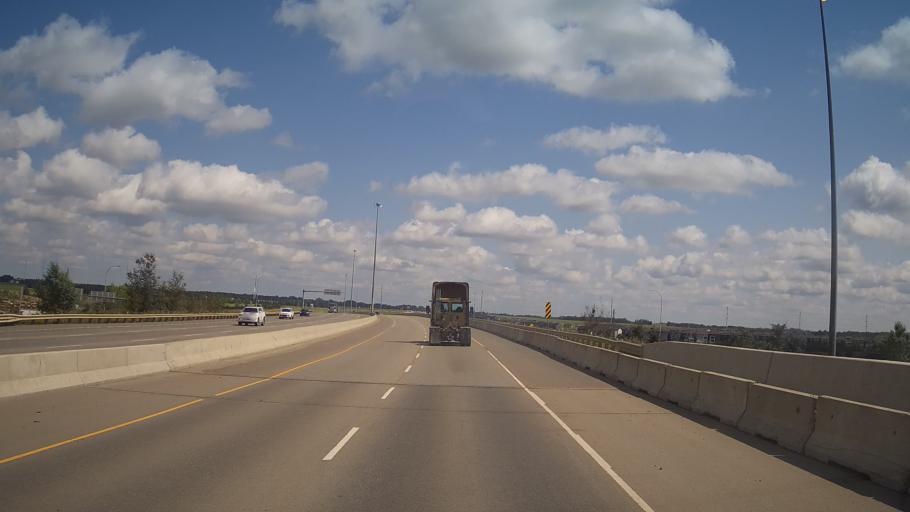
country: CA
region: Alberta
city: Sherwood Park
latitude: 53.4820
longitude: -113.3688
